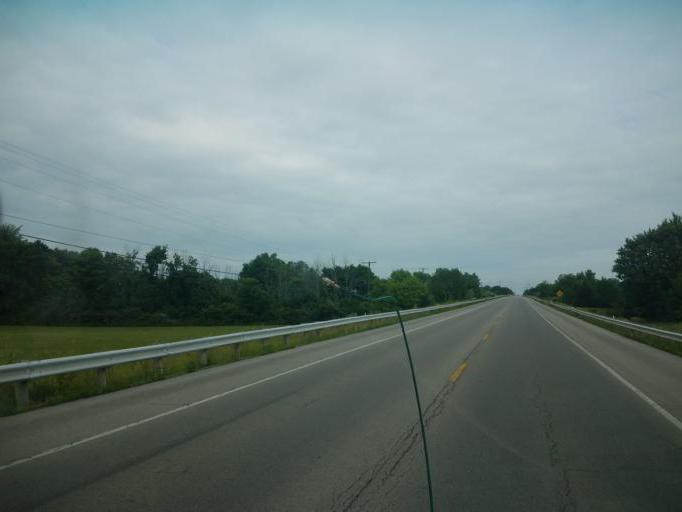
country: US
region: Ohio
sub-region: Hardin County
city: Kenton
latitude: 40.6531
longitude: -83.6275
